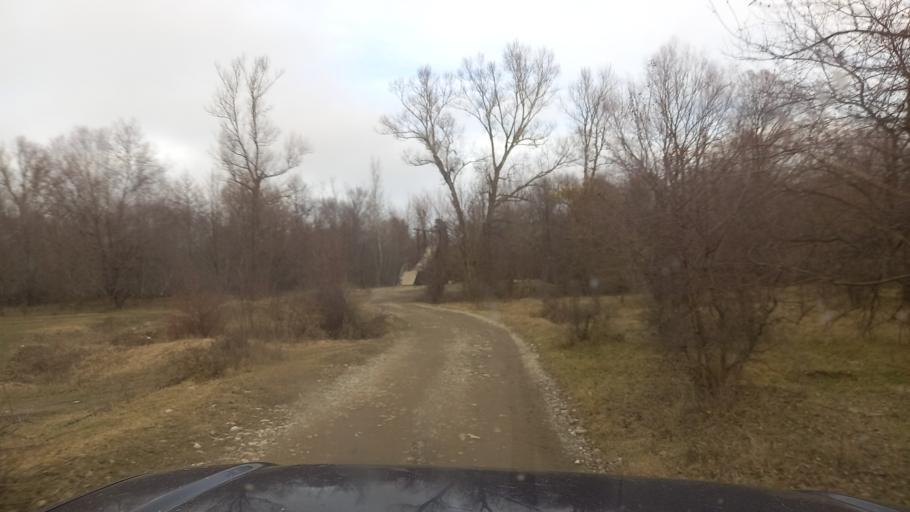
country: RU
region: Krasnodarskiy
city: Neftegorsk
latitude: 44.2431
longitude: 39.7638
